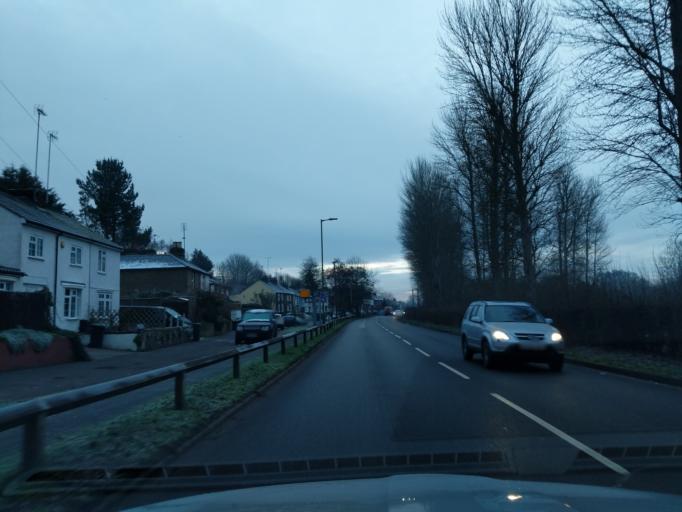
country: GB
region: England
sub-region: Hertfordshire
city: Kings Langley
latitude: 51.7216
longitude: -0.4468
